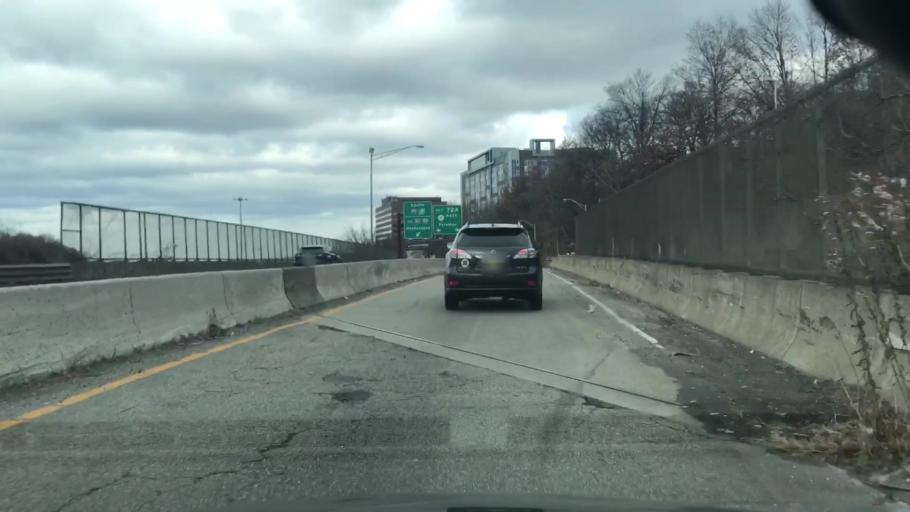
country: US
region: New Jersey
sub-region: Bergen County
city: Fort Lee
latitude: 40.8599
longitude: -73.9747
